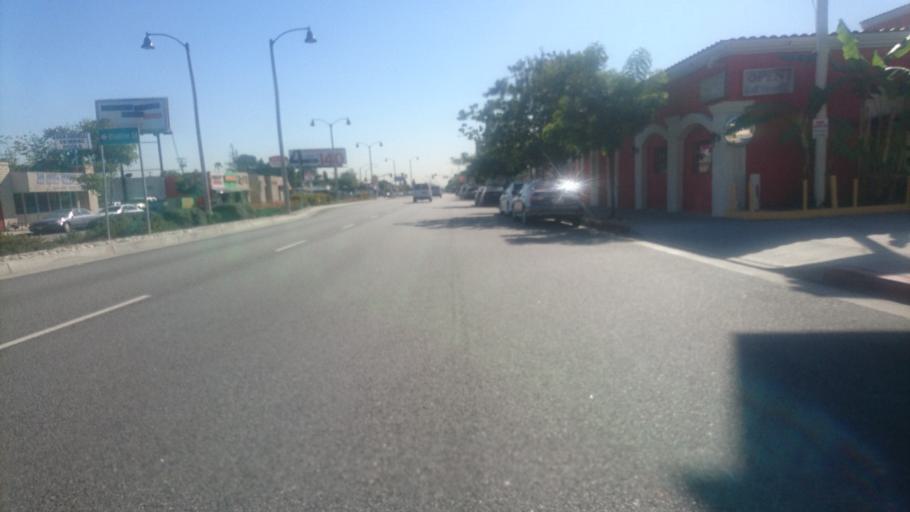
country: US
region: California
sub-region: Los Angeles County
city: East Pasadena
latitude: 34.1439
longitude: -118.0735
